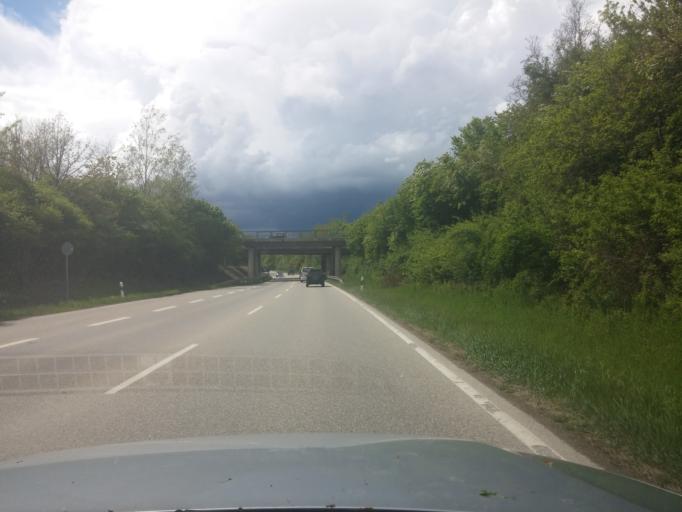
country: DE
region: Bavaria
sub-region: Upper Bavaria
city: Oberhaching
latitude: 48.0344
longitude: 11.5939
